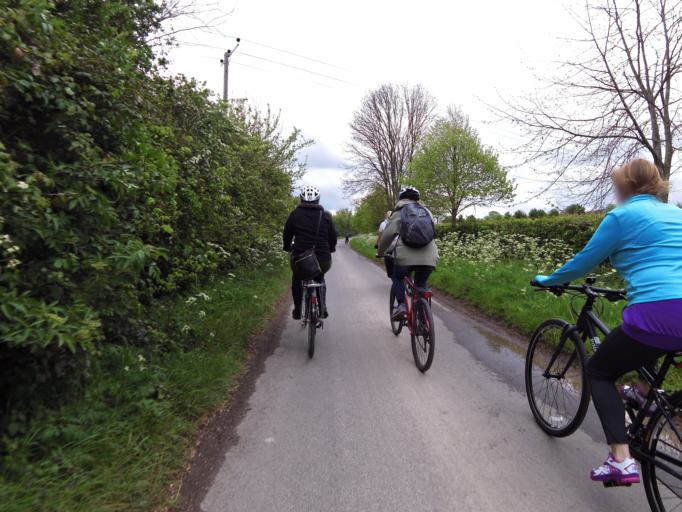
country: GB
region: England
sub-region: Cambridgeshire
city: Bottisham
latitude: 52.2697
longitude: 0.2874
